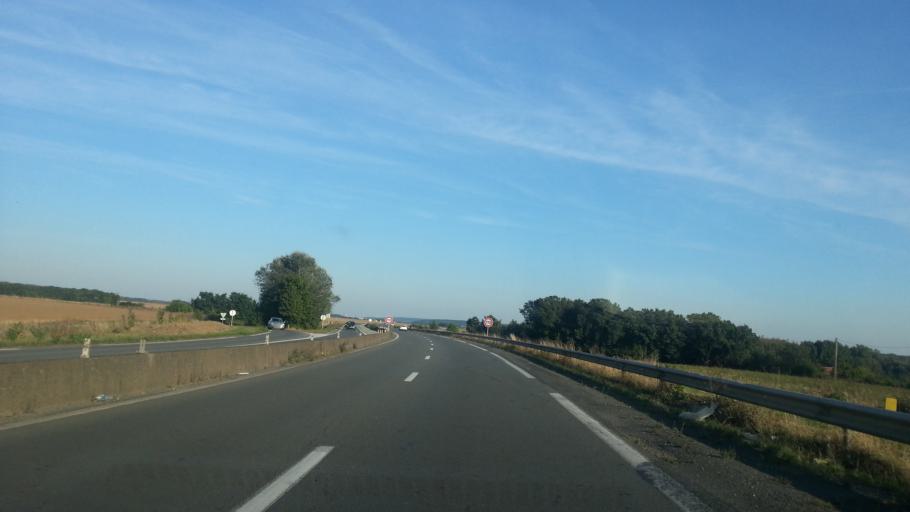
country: FR
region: Picardie
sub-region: Departement de l'Oise
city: Allonne
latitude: 49.4264
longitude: 2.1321
